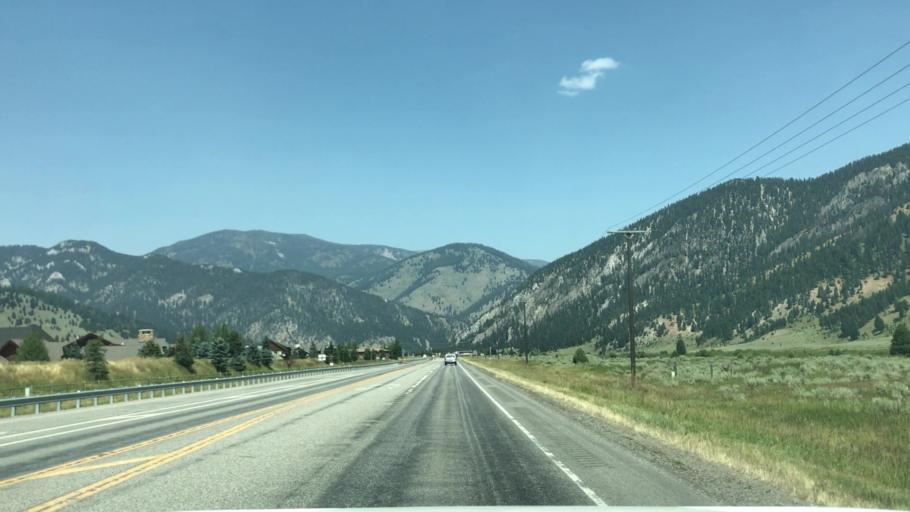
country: US
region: Montana
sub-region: Gallatin County
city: Big Sky
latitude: 45.2402
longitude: -111.2508
